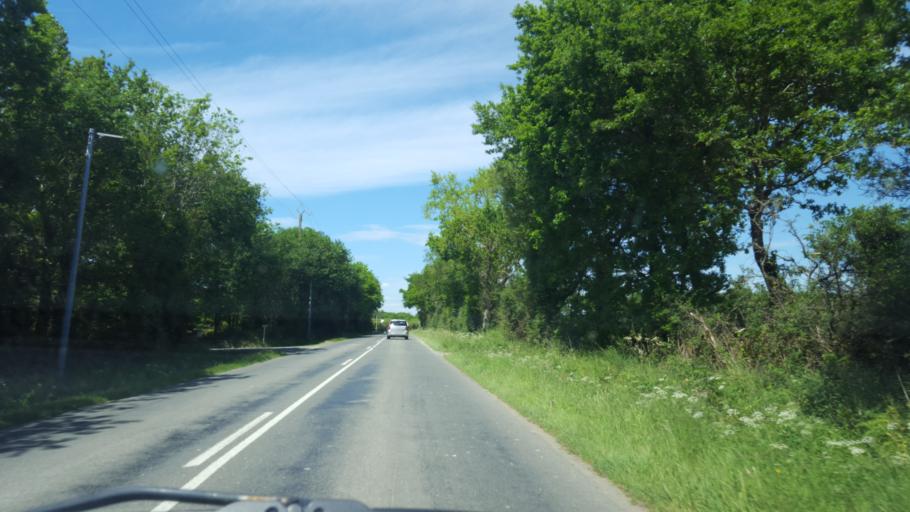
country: FR
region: Pays de la Loire
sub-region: Departement de la Loire-Atlantique
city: Saint-Philbert-de-Grand-Lieu
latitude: 47.0009
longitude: -1.6626
